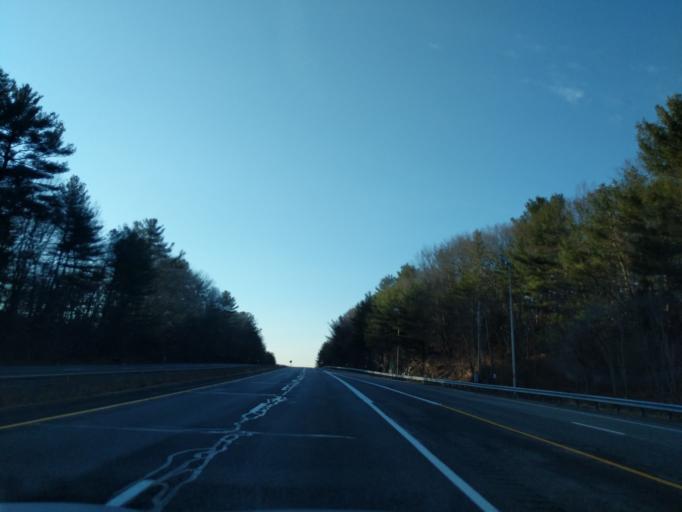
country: US
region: Massachusetts
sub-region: Worcester County
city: Millville
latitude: 42.0066
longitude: -71.5675
